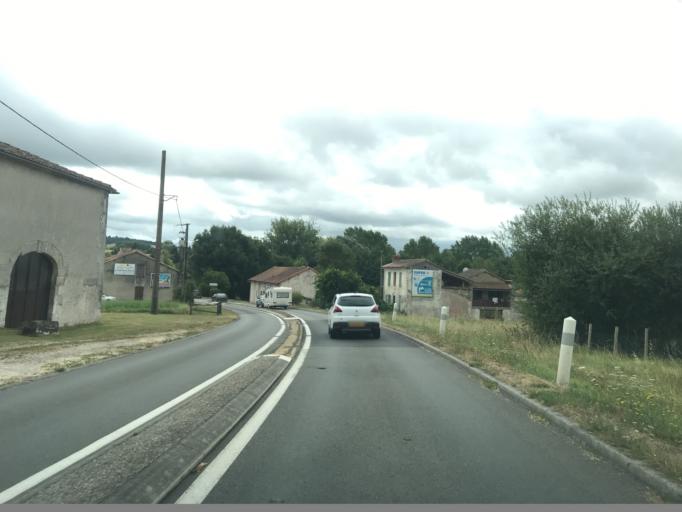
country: FR
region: Poitou-Charentes
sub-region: Departement de la Charente
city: Dignac
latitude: 45.5201
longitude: 0.3036
